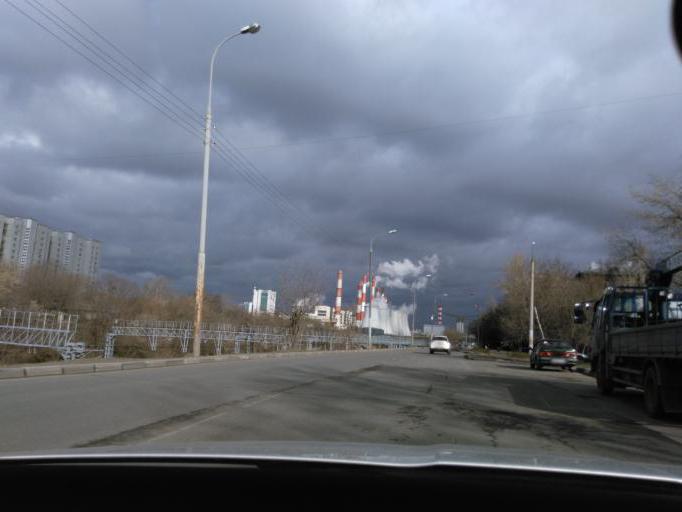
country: RU
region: Moscow
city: Novyye Cheremushki
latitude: 55.6923
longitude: 37.6013
